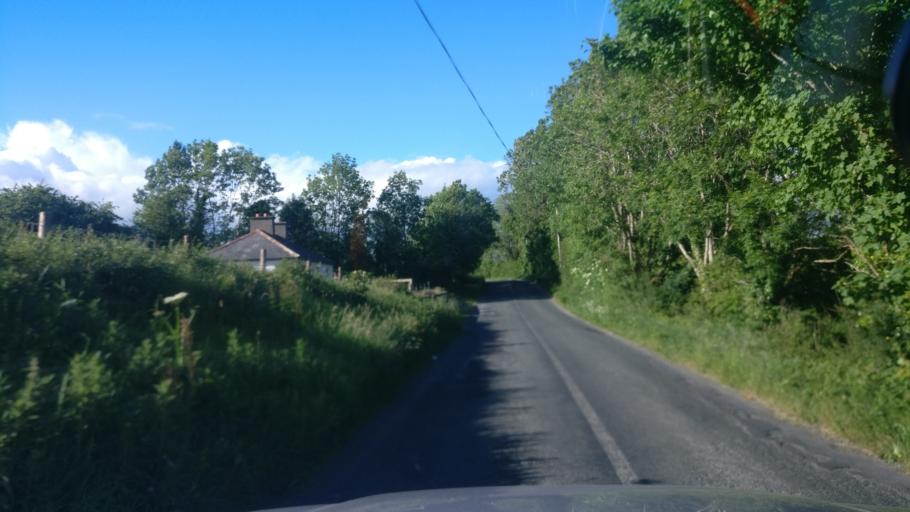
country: IE
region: Connaught
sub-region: County Galway
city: Ballinasloe
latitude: 53.2217
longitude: -8.2920
